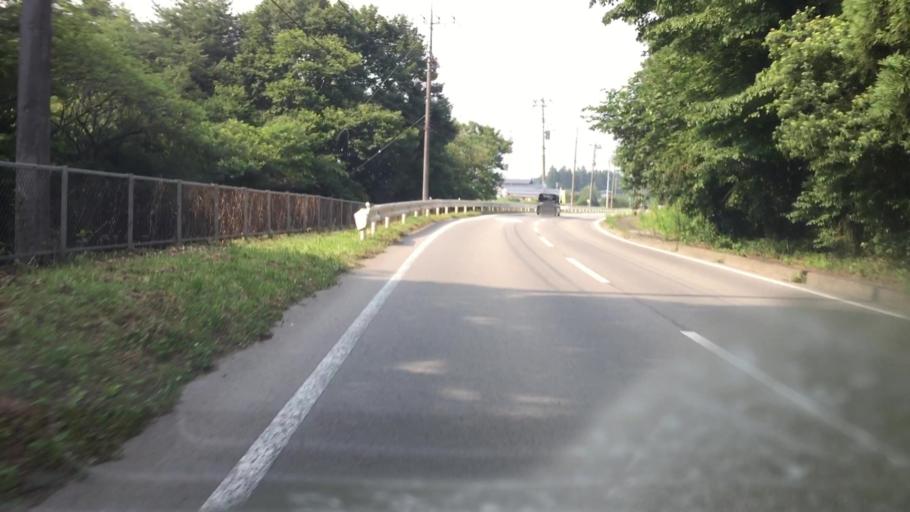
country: JP
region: Tochigi
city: Kuroiso
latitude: 37.0072
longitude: 139.9996
